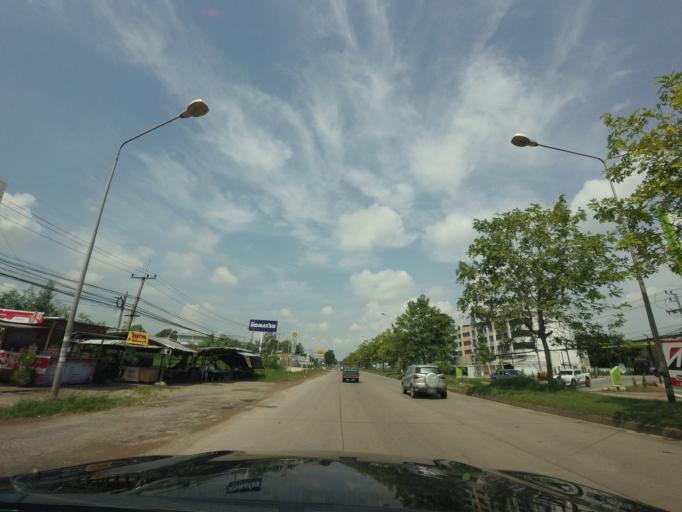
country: TH
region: Khon Kaen
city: Khon Kaen
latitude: 16.4427
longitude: 102.8069
